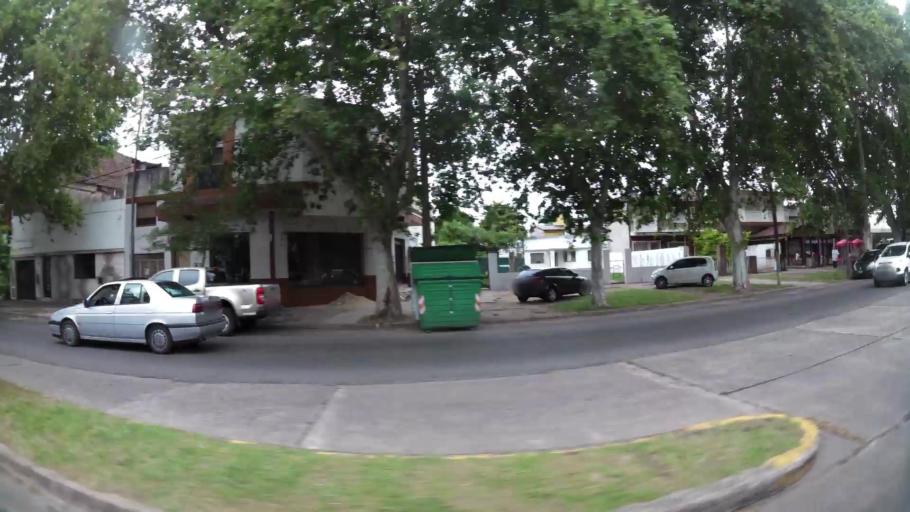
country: AR
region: Santa Fe
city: Granadero Baigorria
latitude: -32.8889
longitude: -60.6940
